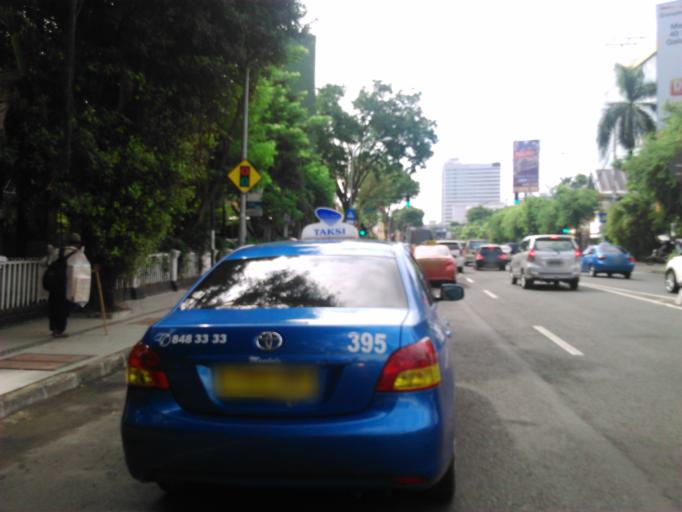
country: ID
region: East Java
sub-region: Kota Surabaya
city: Surabaya
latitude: -7.2628
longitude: 112.7412
